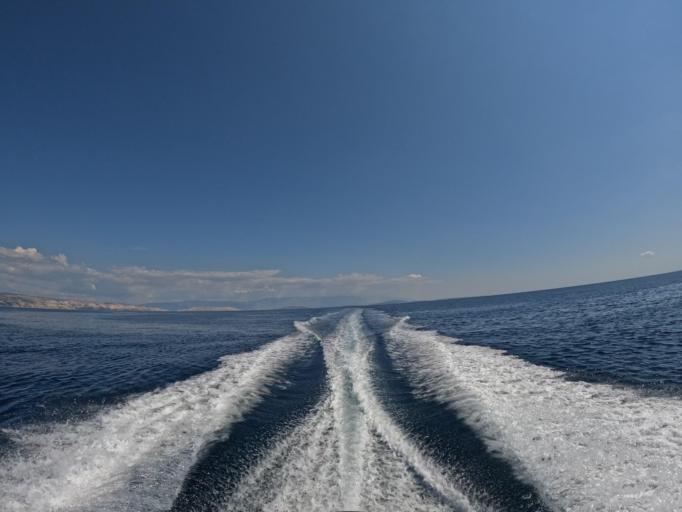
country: HR
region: Primorsko-Goranska
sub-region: Grad Krk
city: Krk
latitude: 44.9318
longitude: 14.5202
